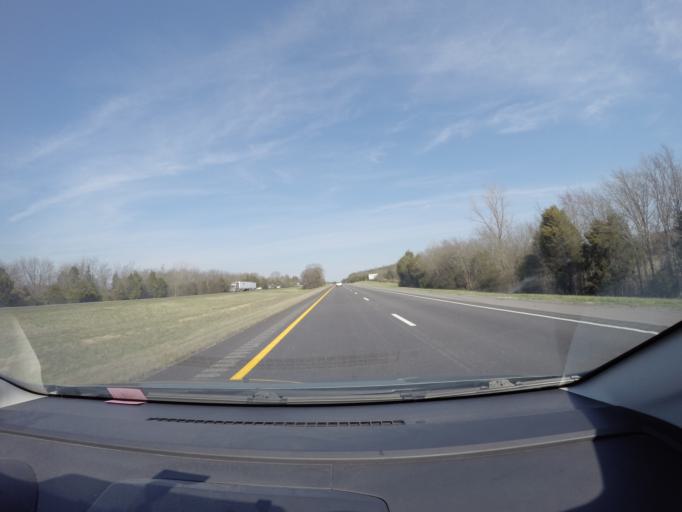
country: US
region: Tennessee
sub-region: Rutherford County
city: Plainview
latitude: 35.6889
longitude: -86.2943
